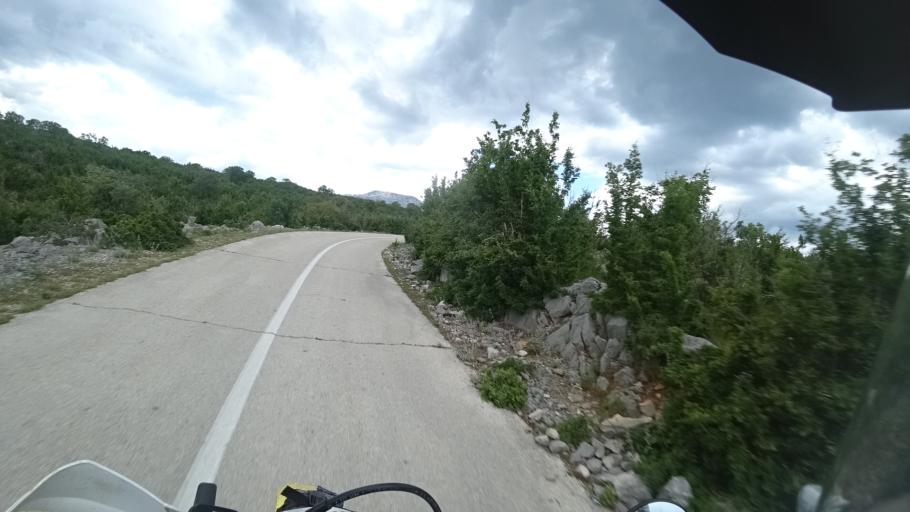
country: HR
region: Zadarska
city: Gracac
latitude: 44.1967
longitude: 15.8739
